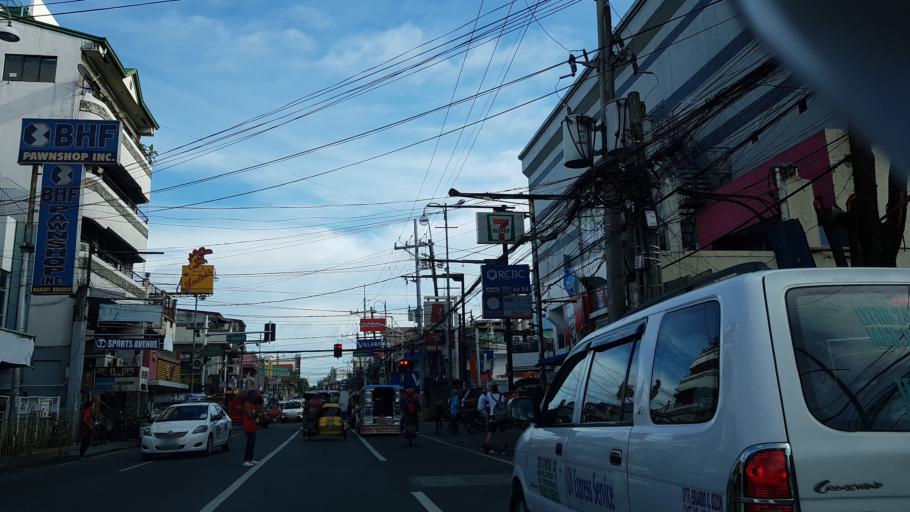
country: PH
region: Calabarzon
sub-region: Province of Rizal
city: Pateros
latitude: 14.5490
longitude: 121.0638
